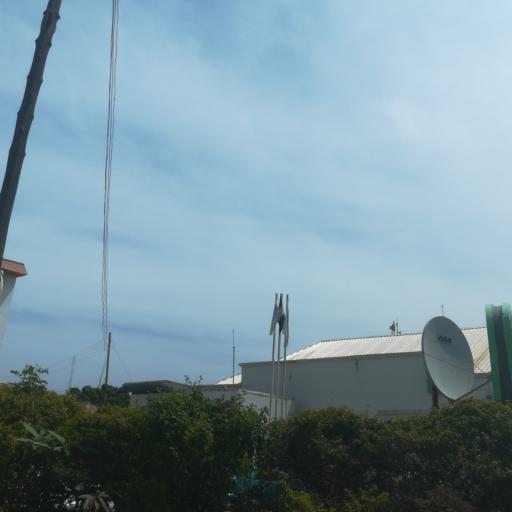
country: NG
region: Plateau
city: Jos
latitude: 9.9097
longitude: 8.8910
